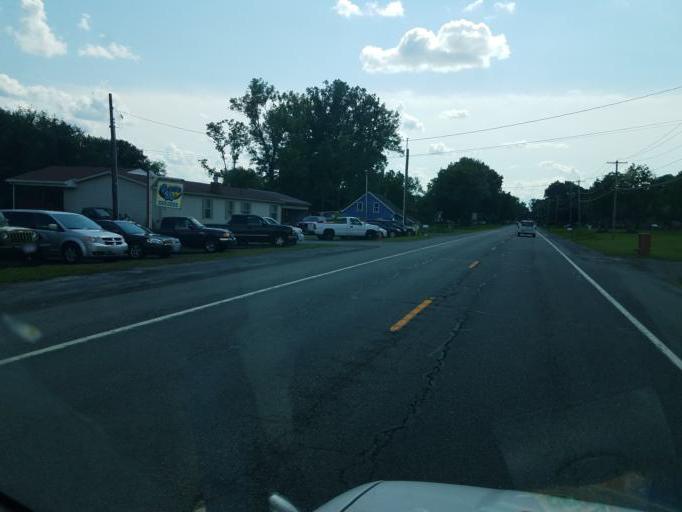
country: US
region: New York
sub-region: Seneca County
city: Waterloo
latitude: 42.8949
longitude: -76.9122
